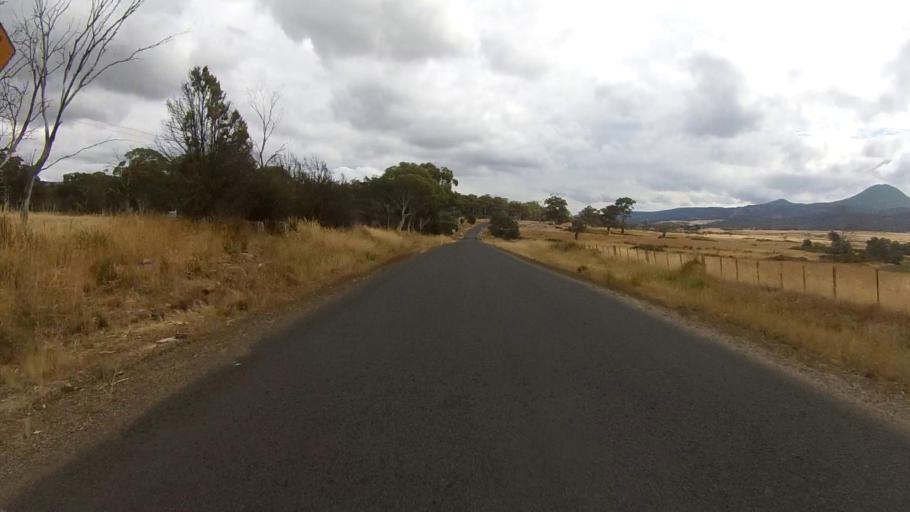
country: AU
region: Tasmania
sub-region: Break O'Day
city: St Helens
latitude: -41.8232
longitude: 147.9191
